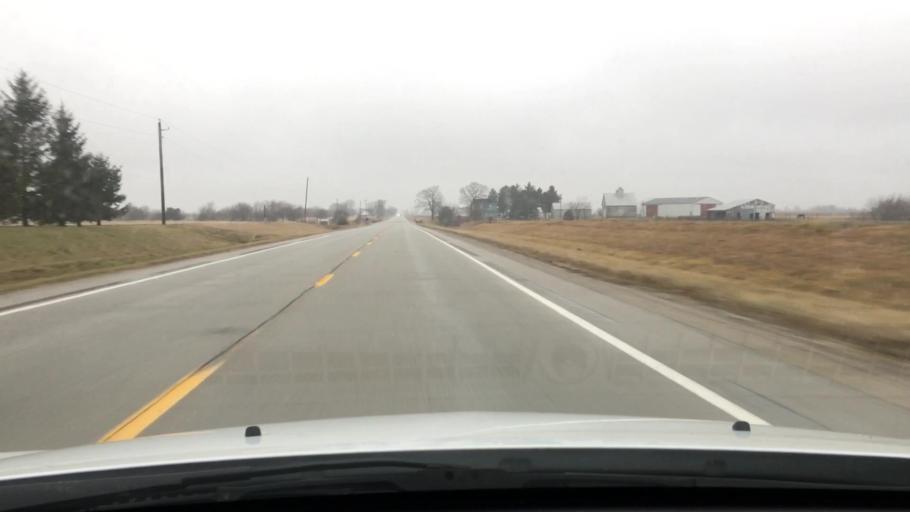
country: US
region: Illinois
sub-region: Livingston County
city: Pontiac
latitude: 40.8726
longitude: -88.7419
